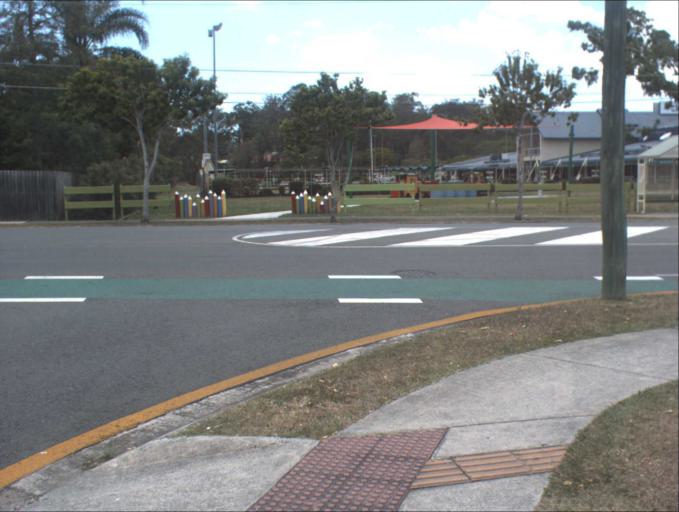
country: AU
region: Queensland
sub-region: Logan
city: Logan City
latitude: -27.6526
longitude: 153.1105
